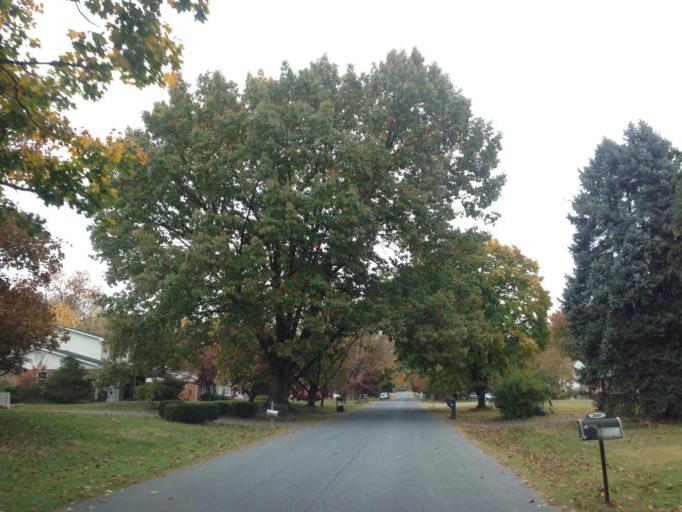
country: US
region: Maryland
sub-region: Howard County
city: Ellicott City
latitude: 39.2992
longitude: -76.8270
